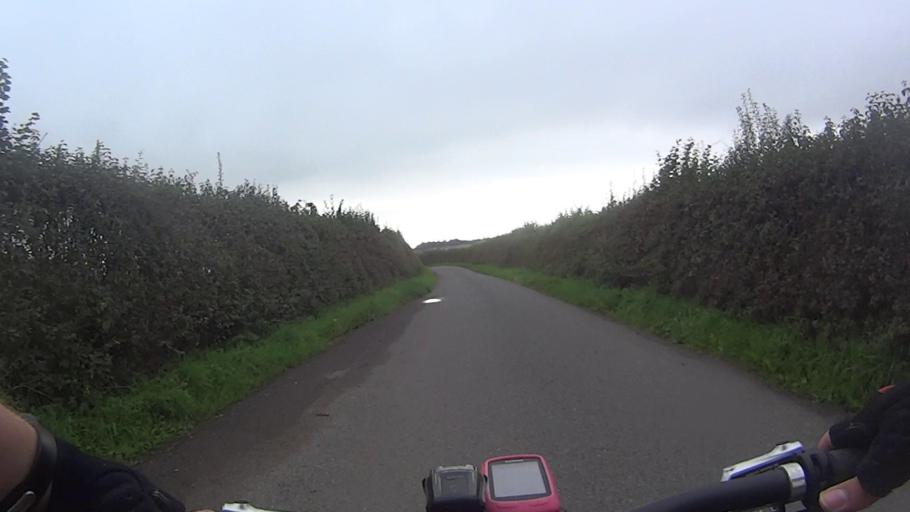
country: GB
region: England
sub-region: Worcestershire
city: Tenbury Wells
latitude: 52.3132
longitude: -2.5712
